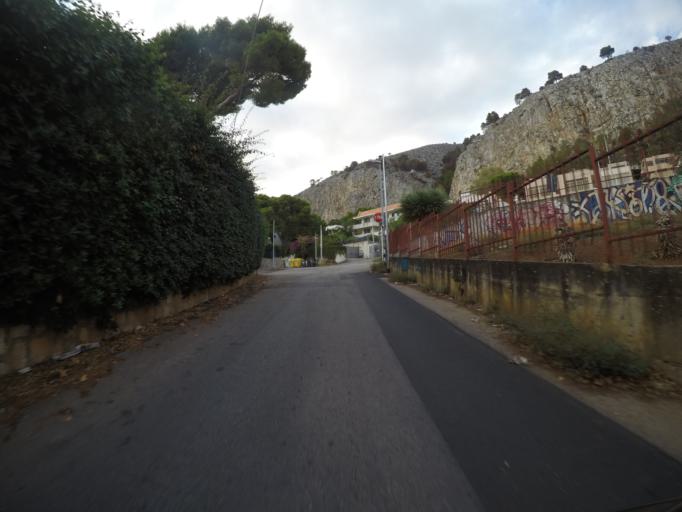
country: IT
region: Sicily
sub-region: Palermo
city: Isola delle Femmine
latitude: 38.2073
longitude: 13.3216
